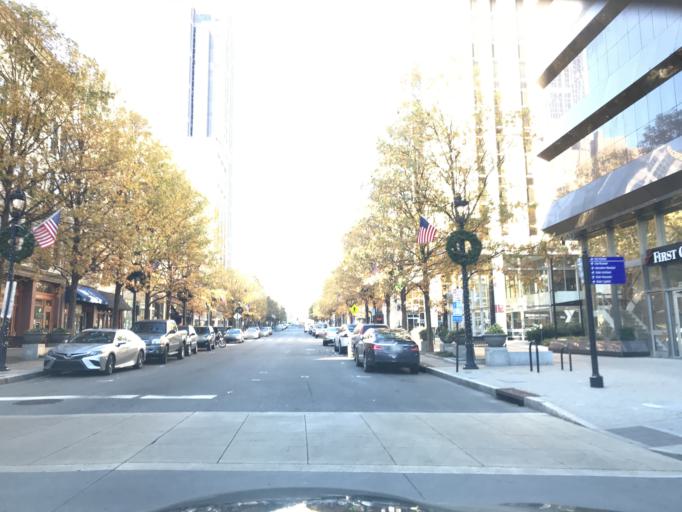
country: US
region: North Carolina
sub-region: Wake County
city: Raleigh
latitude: 35.7769
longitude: -78.6393
